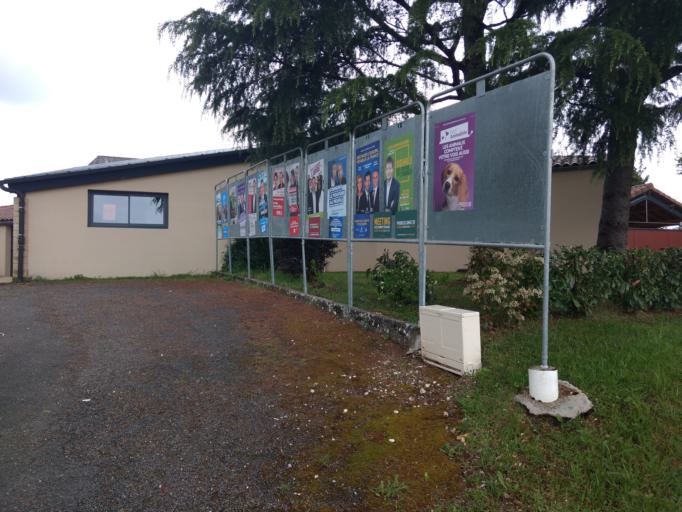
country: FR
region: Midi-Pyrenees
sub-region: Departement de l'Aveyron
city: Capdenac-Gare
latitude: 44.5491
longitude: 2.1094
